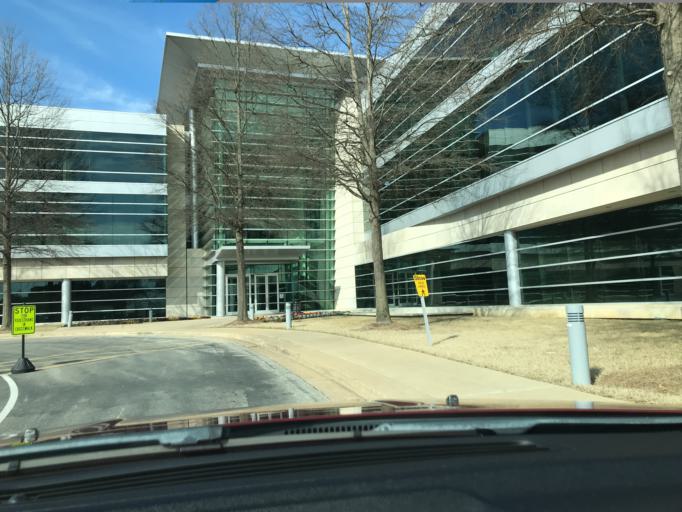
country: US
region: Tennessee
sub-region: Shelby County
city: Germantown
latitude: 35.0504
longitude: -89.7902
